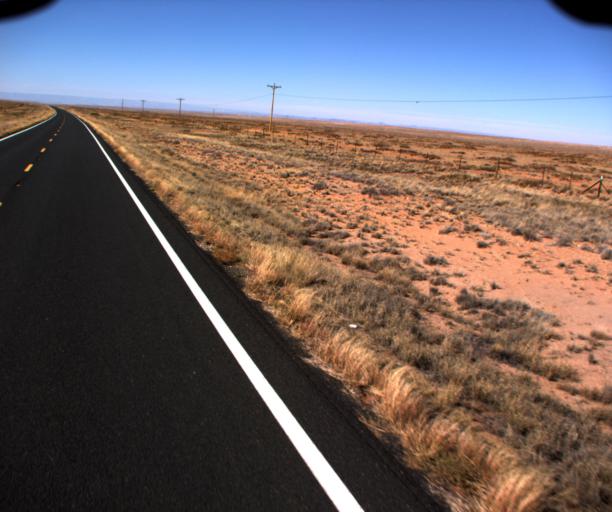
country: US
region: Arizona
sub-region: Coconino County
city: Tuba City
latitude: 36.0091
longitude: -111.0617
